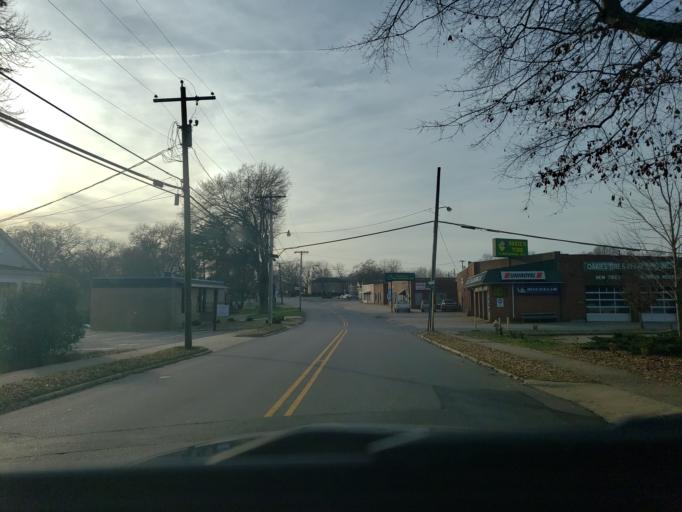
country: US
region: North Carolina
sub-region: Cleveland County
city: Shelby
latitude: 35.2912
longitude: -81.5527
